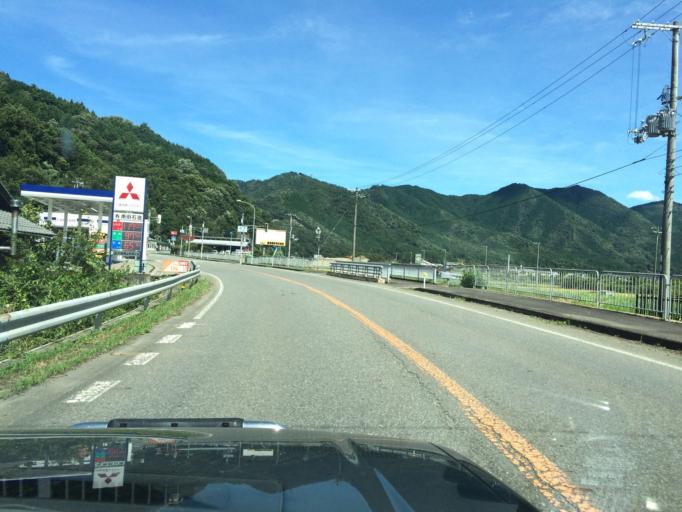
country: JP
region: Hyogo
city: Toyooka
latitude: 35.3843
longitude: 134.7867
